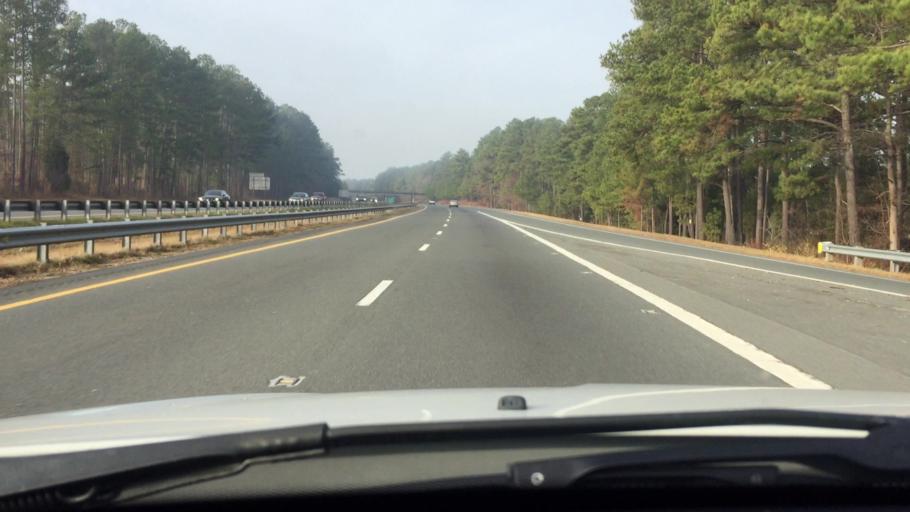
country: US
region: North Carolina
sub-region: Wake County
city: Green Level
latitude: 35.6448
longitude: -79.0079
